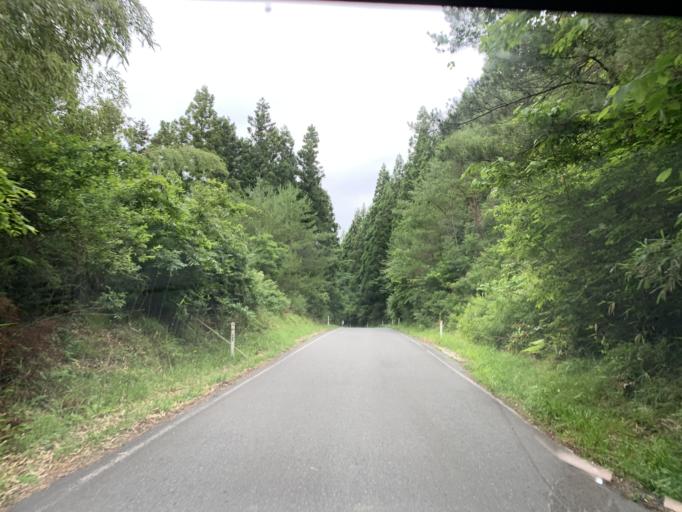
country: JP
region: Iwate
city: Ichinoseki
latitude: 38.8260
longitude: 141.2326
